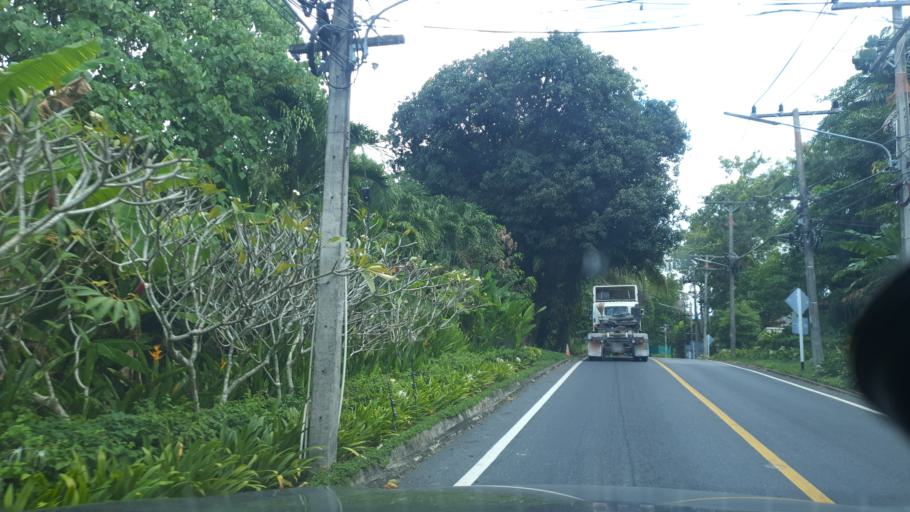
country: TH
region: Phuket
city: Thalang
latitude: 8.0394
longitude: 98.2757
